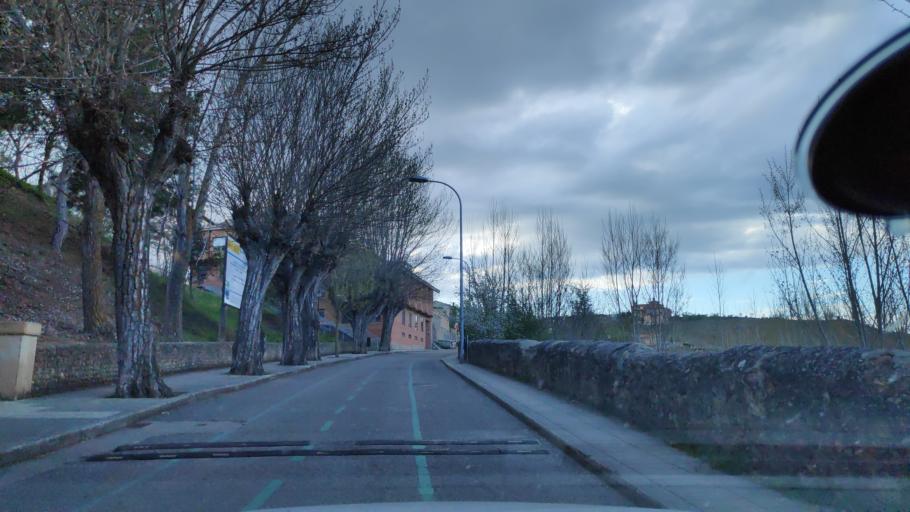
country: ES
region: Castille and Leon
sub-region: Provincia de Soria
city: Soria
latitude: 41.7643
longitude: -2.4557
